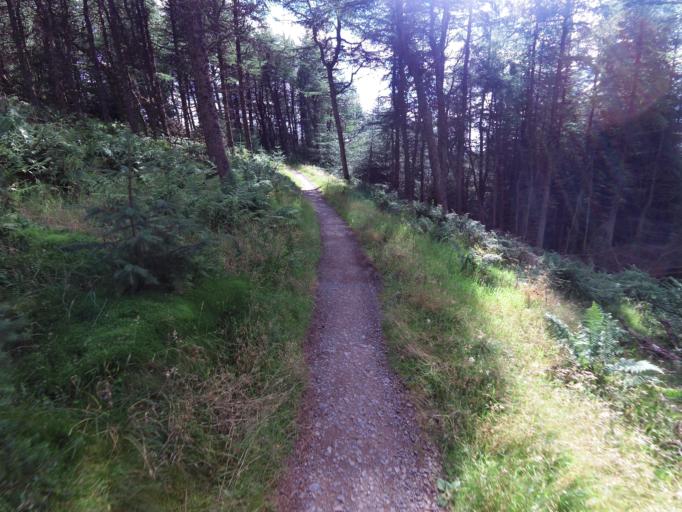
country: GB
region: Scotland
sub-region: The Scottish Borders
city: Peebles
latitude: 55.6717
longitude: -3.1341
